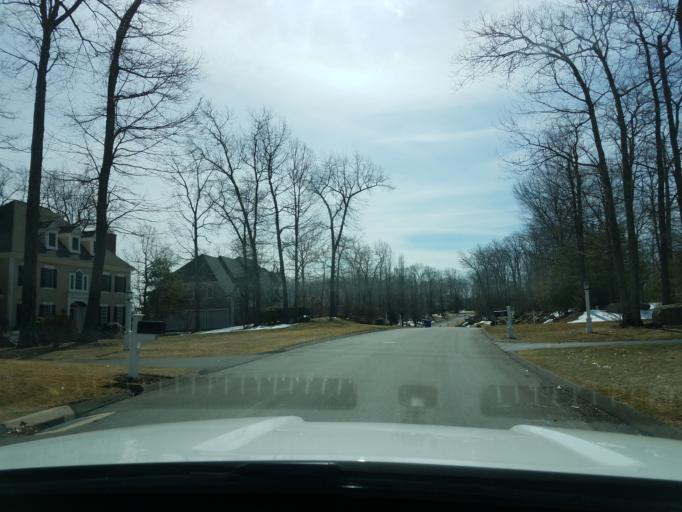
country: US
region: Connecticut
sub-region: Hartford County
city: Collinsville
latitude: 41.7974
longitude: -72.9010
